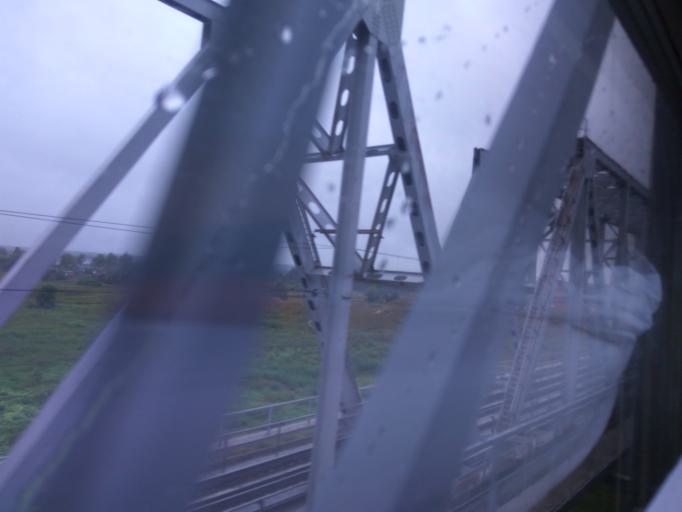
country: RU
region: Moskovskaya
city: Kashira
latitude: 54.8622
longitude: 38.1641
